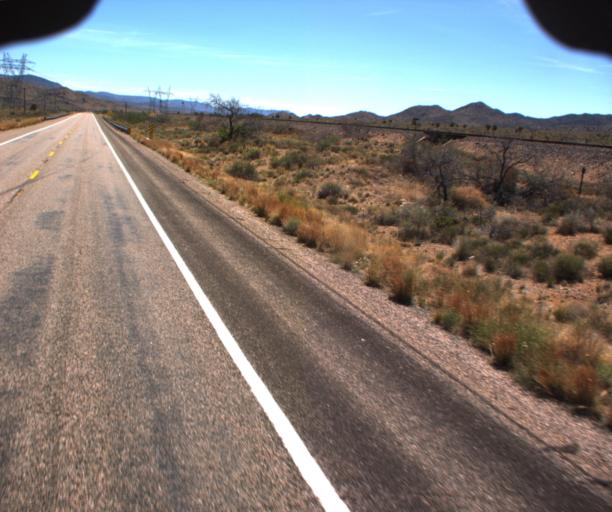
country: US
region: Arizona
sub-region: Mohave County
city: New Kingman-Butler
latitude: 35.3998
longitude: -113.7584
